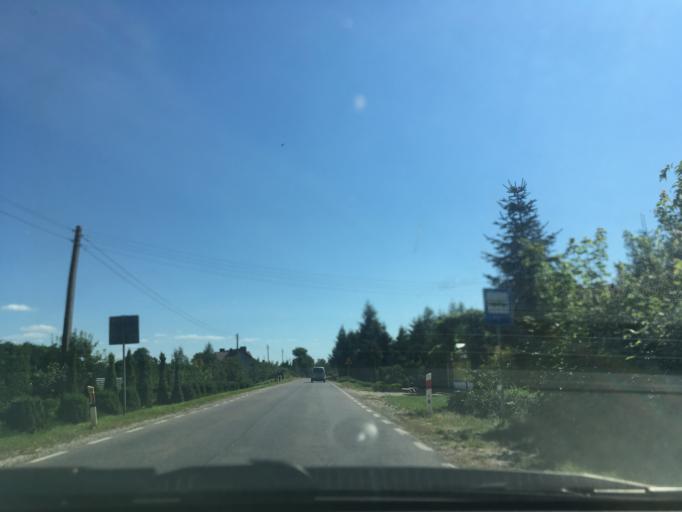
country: PL
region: Podlasie
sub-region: Powiat suwalski
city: Raczki
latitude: 53.9505
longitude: 22.8290
